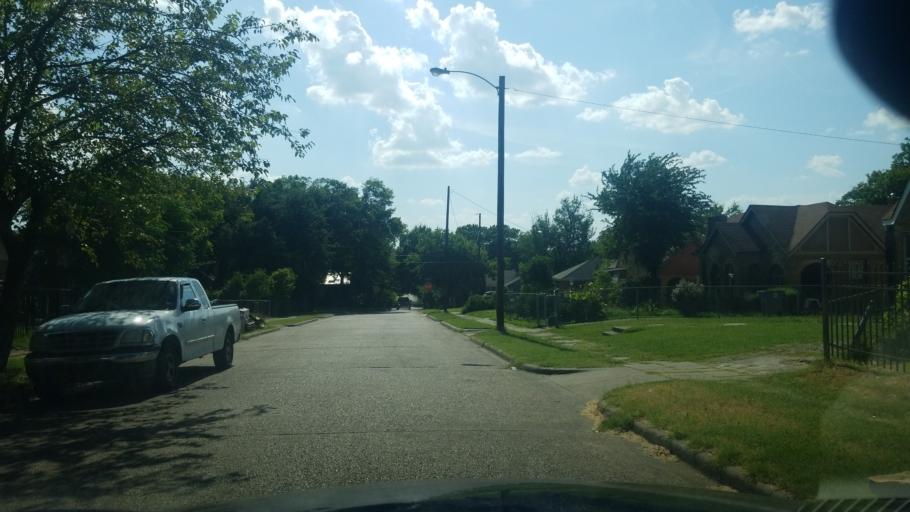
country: US
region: Texas
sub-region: Dallas County
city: Dallas
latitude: 32.7239
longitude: -96.8068
